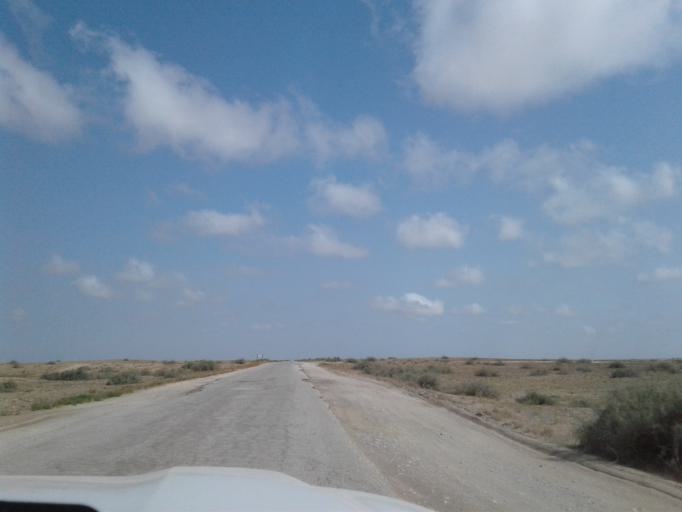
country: IR
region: Golestan
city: Gomishan
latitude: 37.6313
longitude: 53.9289
